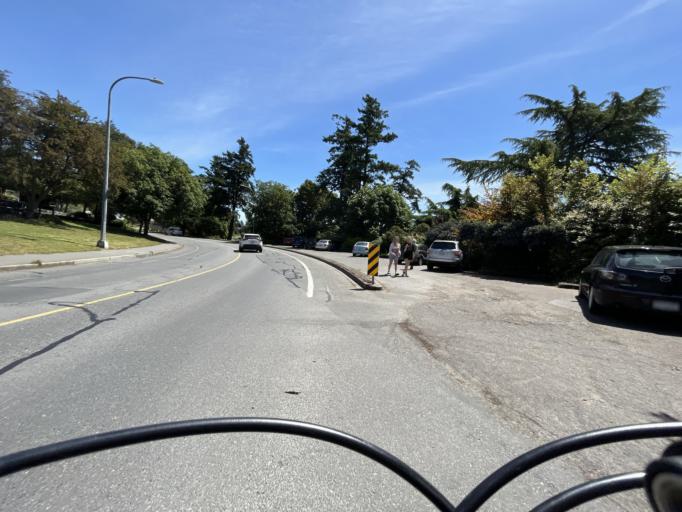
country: CA
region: British Columbia
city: Victoria
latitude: 48.4504
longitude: -123.4134
